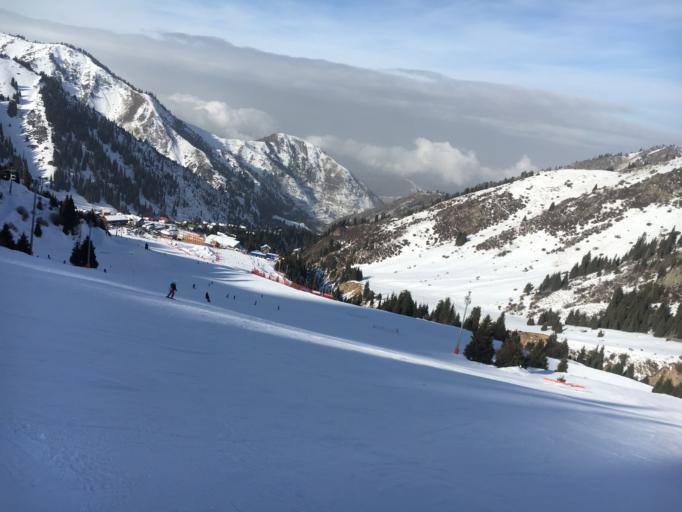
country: KZ
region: Almaty Qalasy
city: Almaty
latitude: 43.1236
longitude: 77.0925
